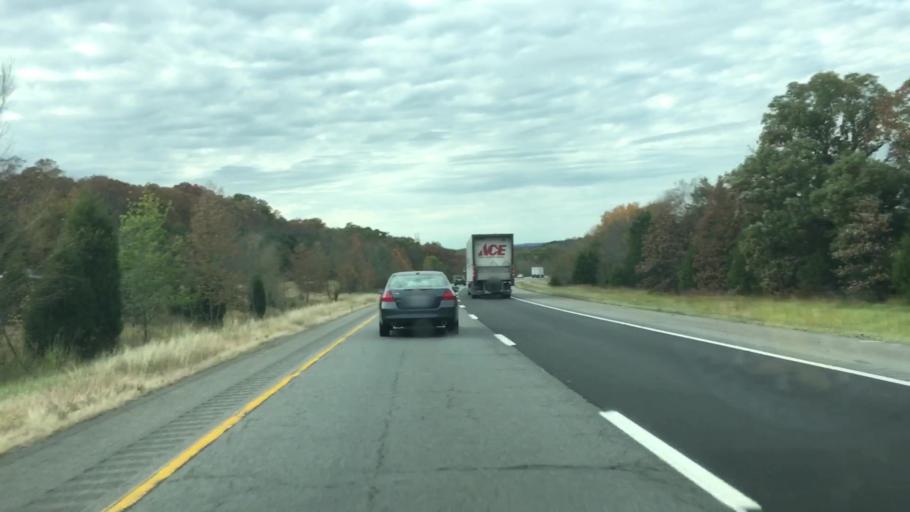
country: US
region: Arkansas
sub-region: Faulkner County
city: Conway
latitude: 35.1234
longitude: -92.5039
